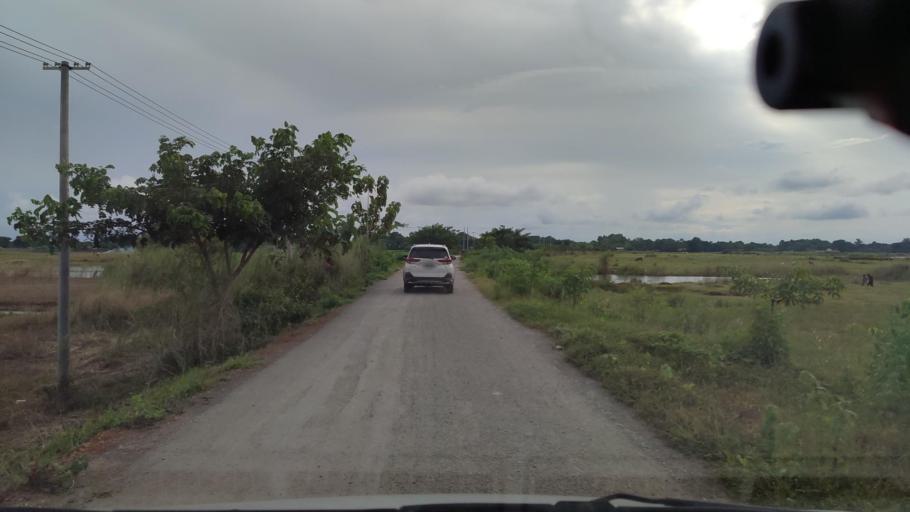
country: MM
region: Bago
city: Tharyarwady
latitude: 17.5991
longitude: 95.7240
